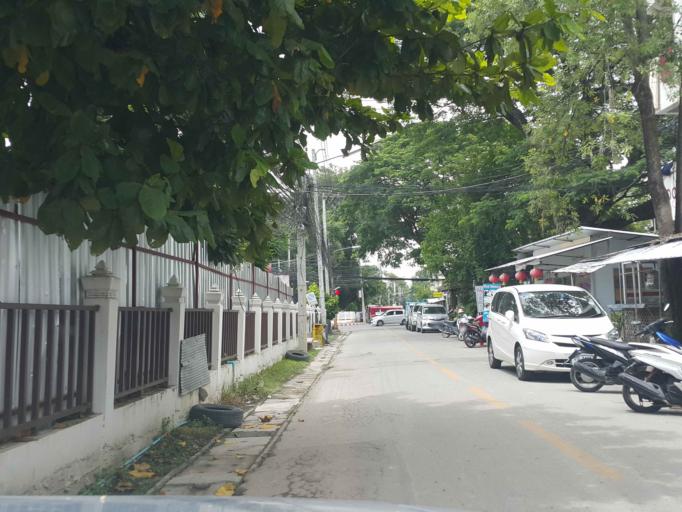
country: TH
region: Chiang Mai
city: Chiang Mai
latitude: 18.7876
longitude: 98.9851
